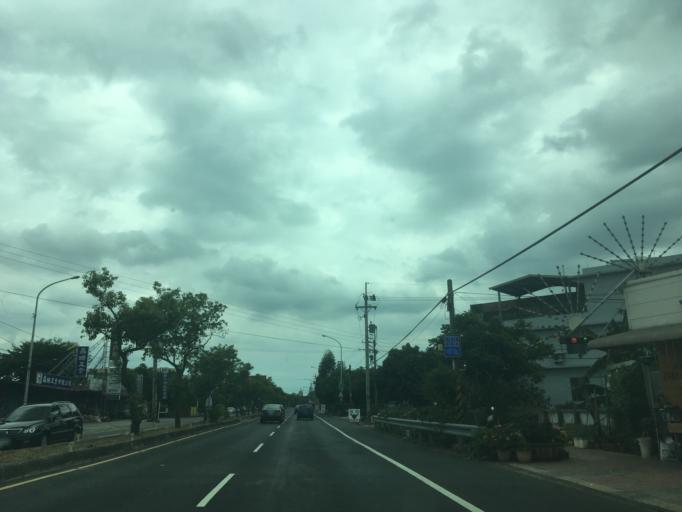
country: TW
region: Taiwan
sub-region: Hsinchu
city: Zhubei
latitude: 24.7635
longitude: 121.0879
